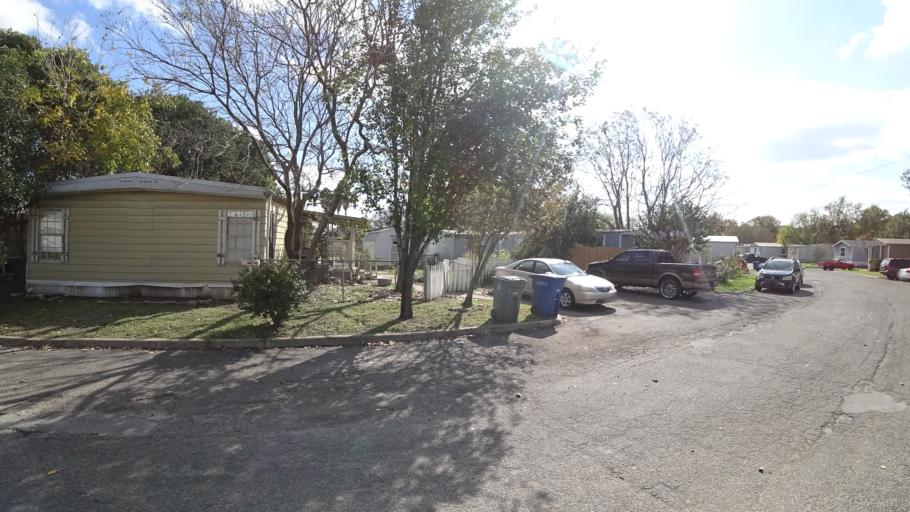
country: US
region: Texas
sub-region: Travis County
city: Barton Creek
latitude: 30.2485
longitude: -97.8870
